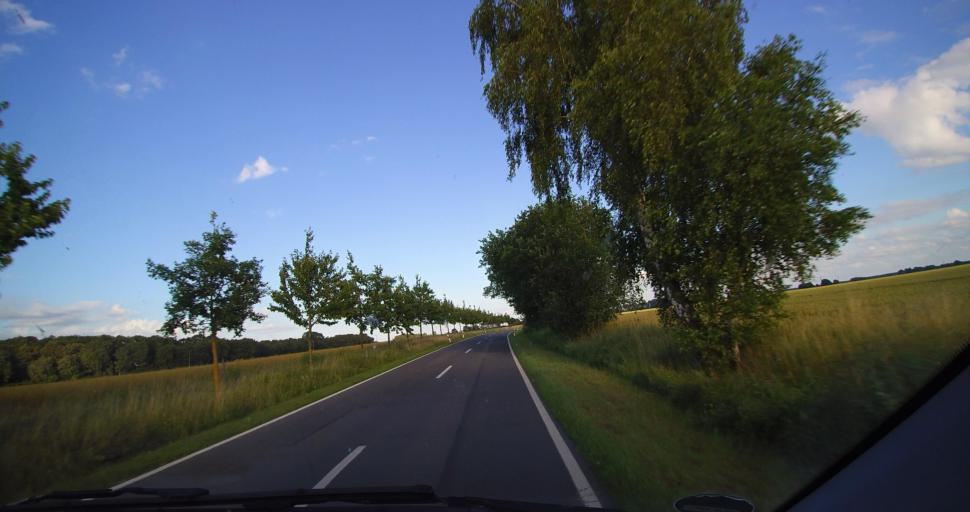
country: DE
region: Mecklenburg-Vorpommern
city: Franzburg
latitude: 54.2195
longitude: 12.8497
